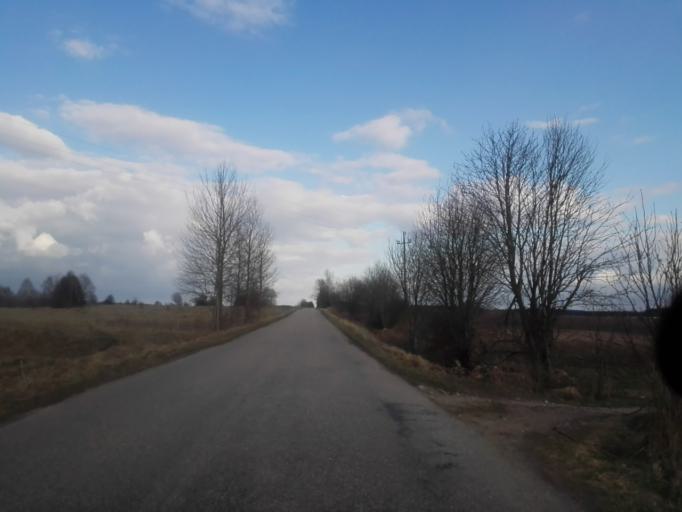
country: PL
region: Podlasie
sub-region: Suwalki
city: Suwalki
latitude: 54.2215
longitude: 22.8371
